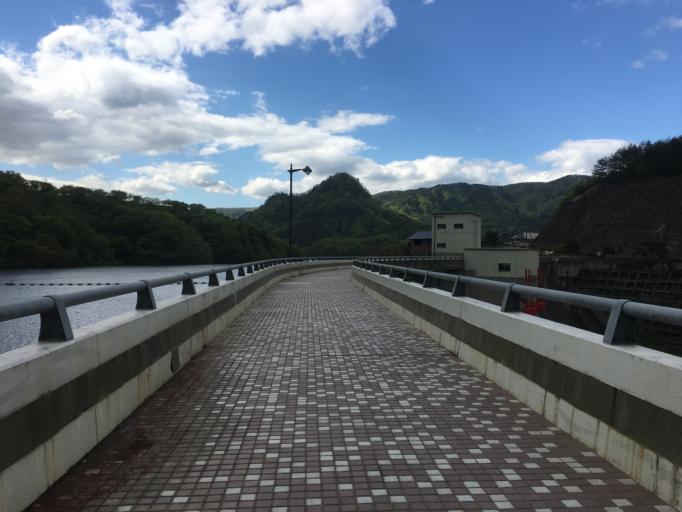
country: JP
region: Miyagi
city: Marumori
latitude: 37.7177
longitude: 140.8335
